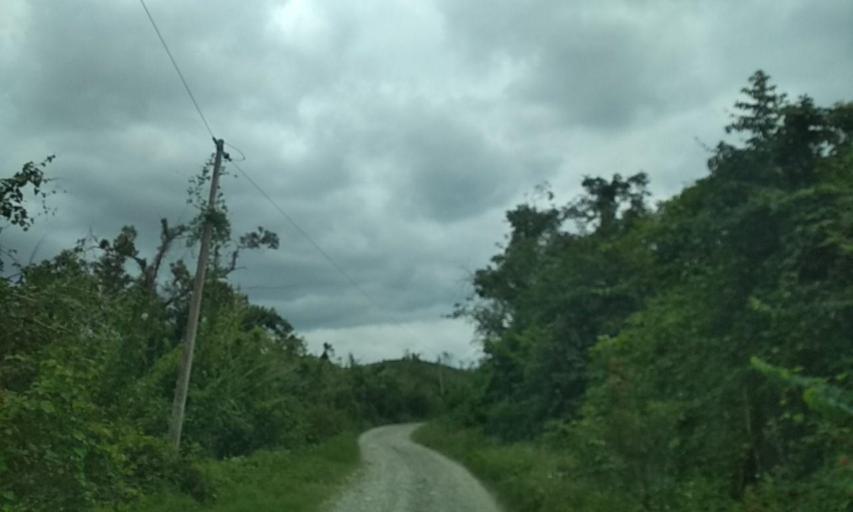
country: MX
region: Veracruz
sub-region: Papantla
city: Polutla
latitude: 20.5228
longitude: -97.2984
